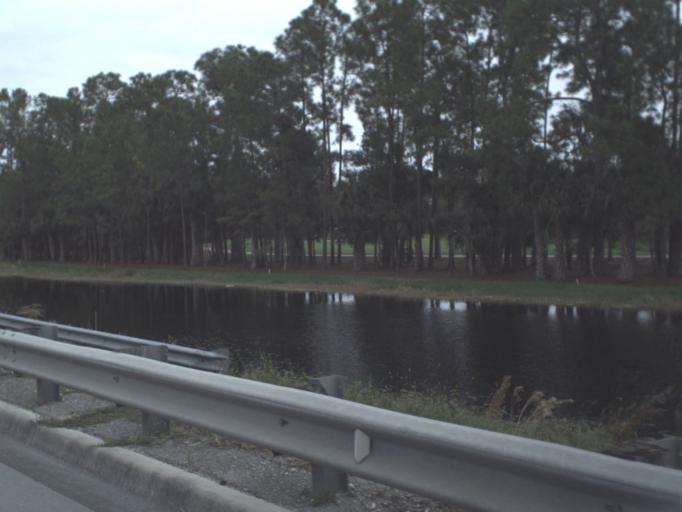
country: US
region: Florida
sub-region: Collier County
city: Golden Gate
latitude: 26.1499
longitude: -81.6866
